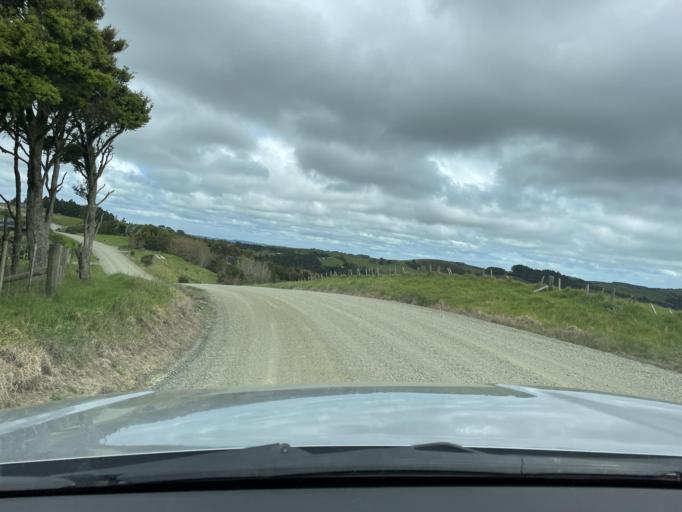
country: NZ
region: Auckland
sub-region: Auckland
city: Wellsford
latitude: -36.1668
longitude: 174.5533
